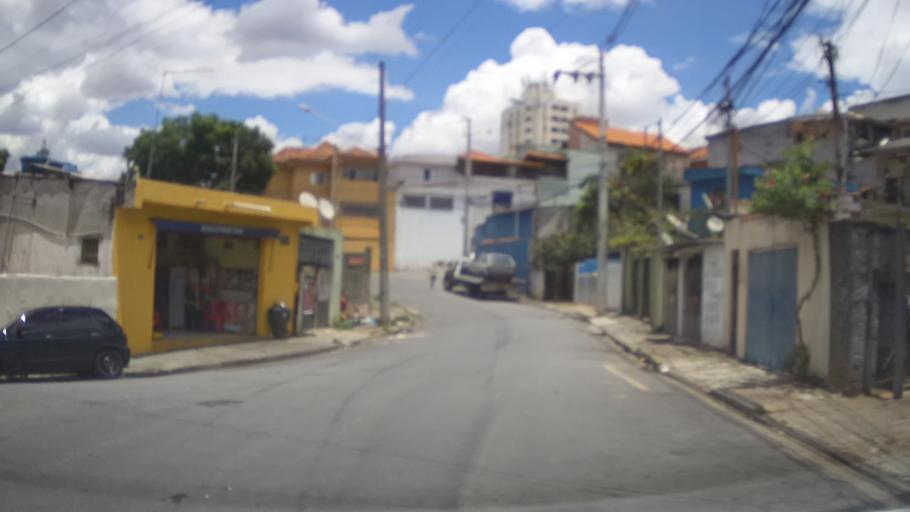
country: BR
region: Sao Paulo
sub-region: Guarulhos
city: Guarulhos
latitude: -23.4592
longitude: -46.5440
